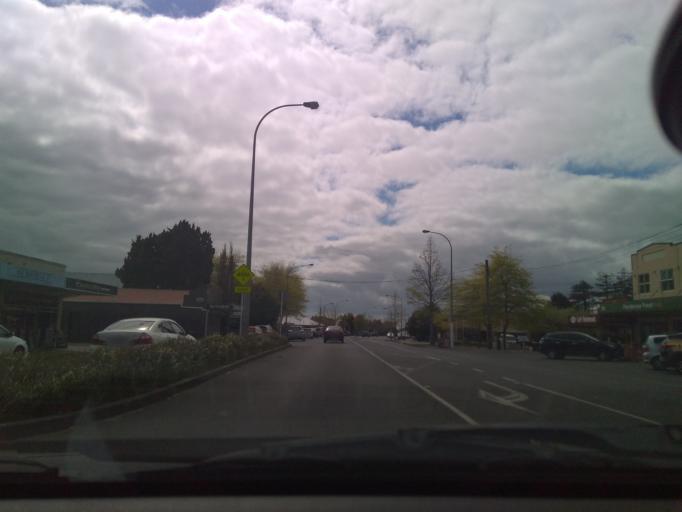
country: NZ
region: Auckland
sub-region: Auckland
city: Rosebank
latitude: -36.8658
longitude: 174.5797
